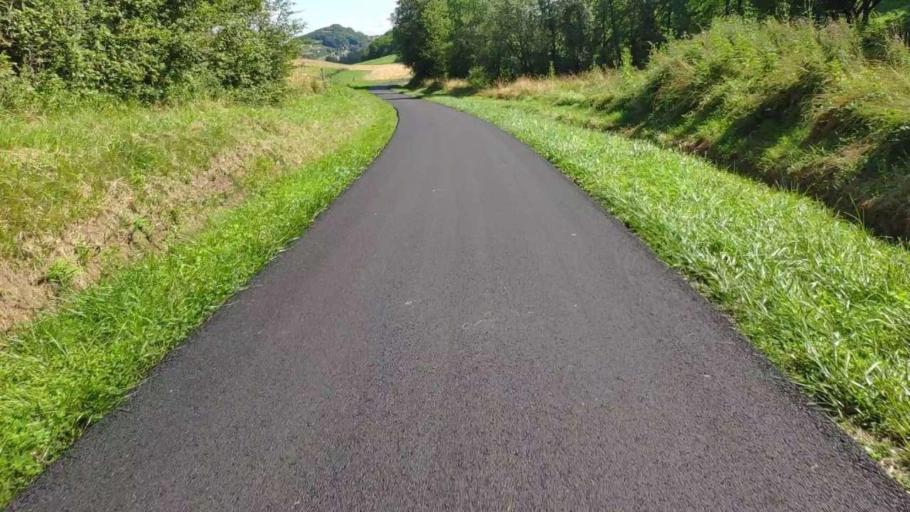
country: FR
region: Franche-Comte
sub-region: Departement du Jura
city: Bletterans
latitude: 46.8016
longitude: 5.5709
